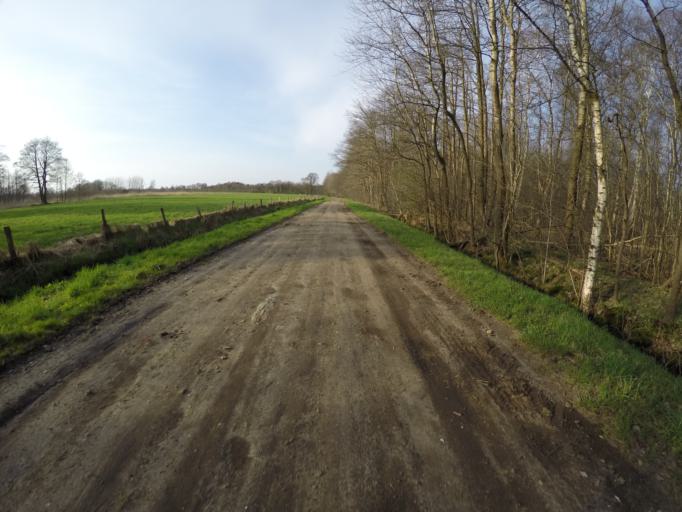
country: DE
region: Schleswig-Holstein
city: Hemdingen
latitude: 53.7346
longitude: 9.8252
